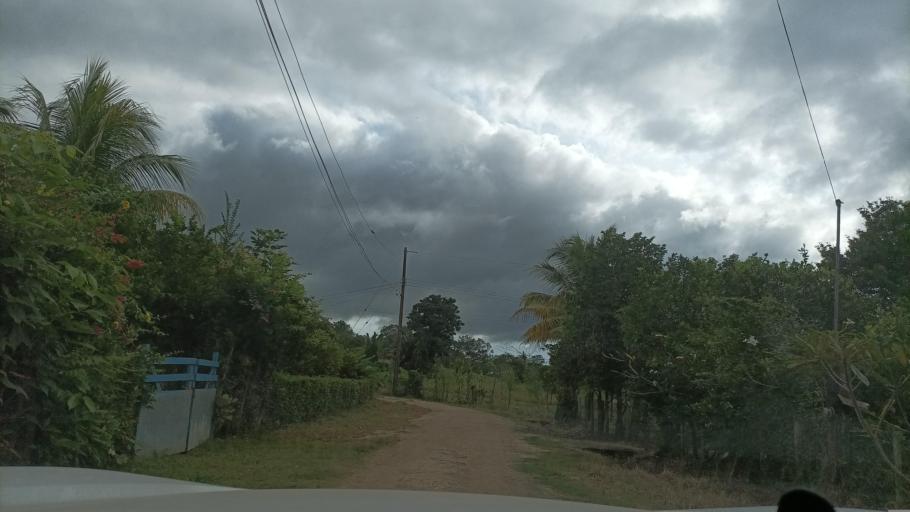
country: MX
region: Veracruz
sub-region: Jaltipan
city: Las Lomas de Tacamichapan
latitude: 17.8635
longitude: -94.7121
